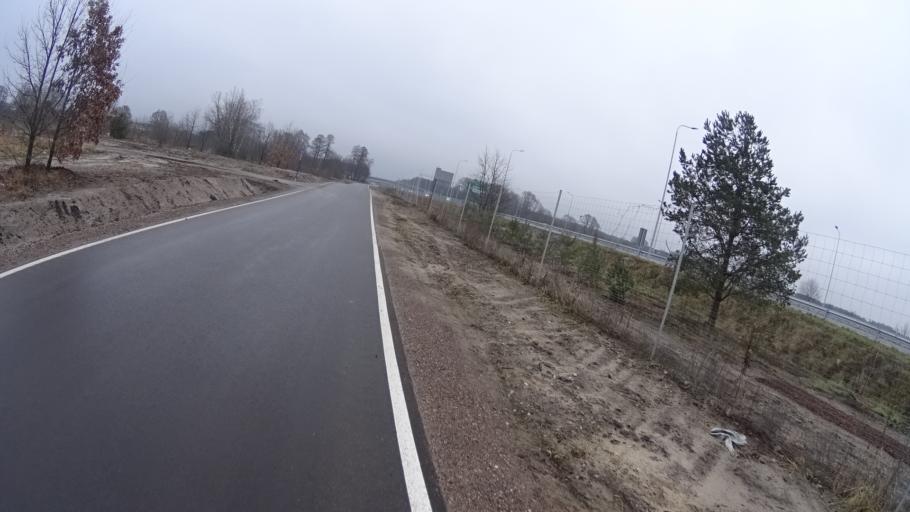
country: PL
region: Masovian Voivodeship
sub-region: Warszawa
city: Wawer
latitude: 52.1654
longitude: 21.1777
